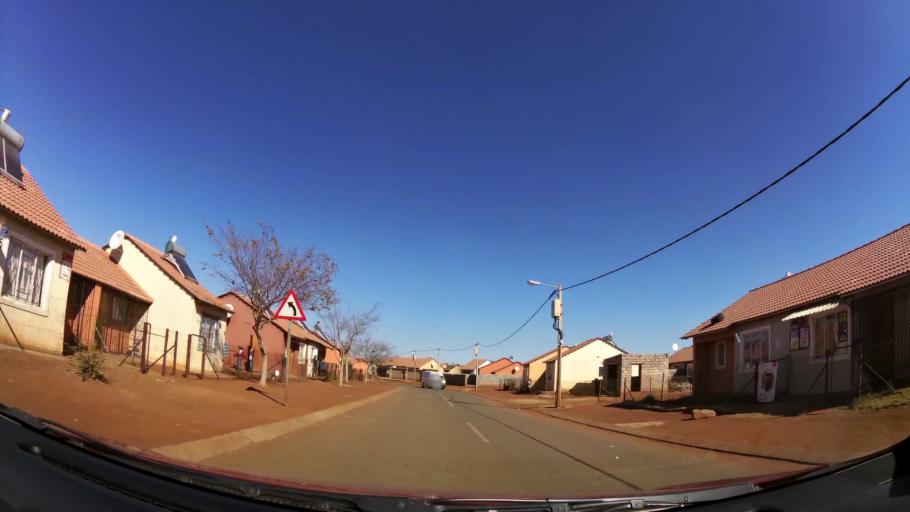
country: ZA
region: Gauteng
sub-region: City of Johannesburg Metropolitan Municipality
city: Soweto
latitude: -26.2344
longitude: 27.7987
